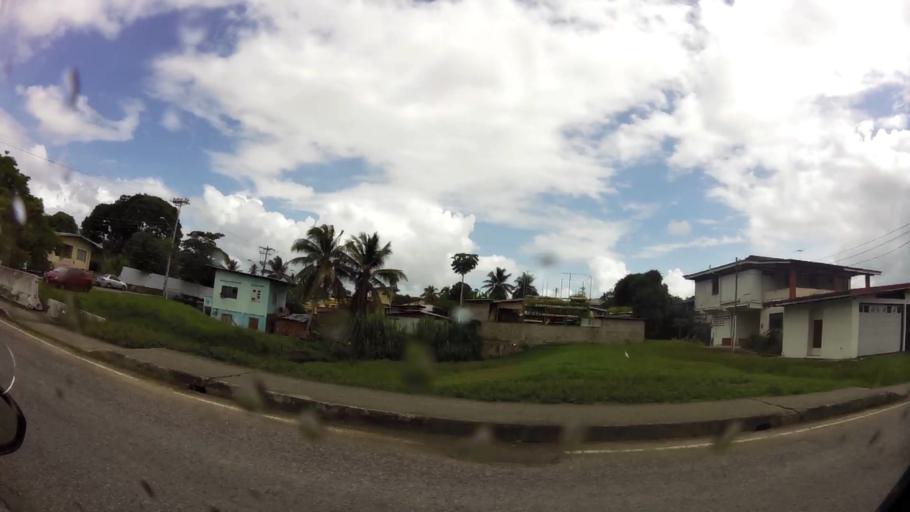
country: TT
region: Tunapuna/Piarco
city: Arouca
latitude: 10.6306
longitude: -61.3388
